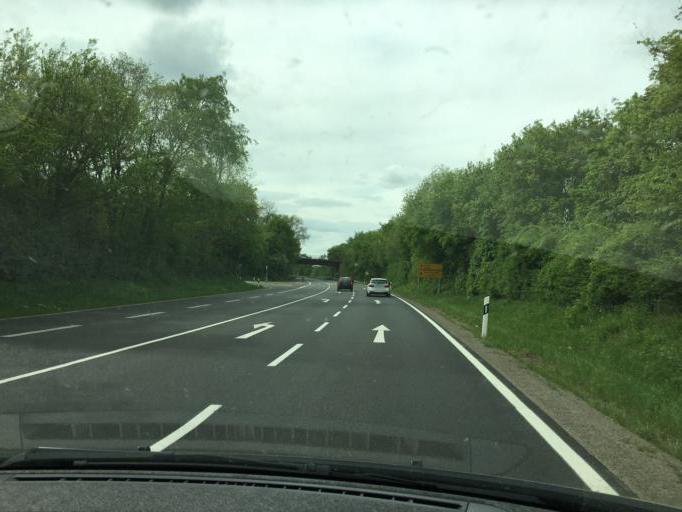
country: DE
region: North Rhine-Westphalia
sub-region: Regierungsbezirk Koln
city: Euskirchen
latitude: 50.6875
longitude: 6.7434
